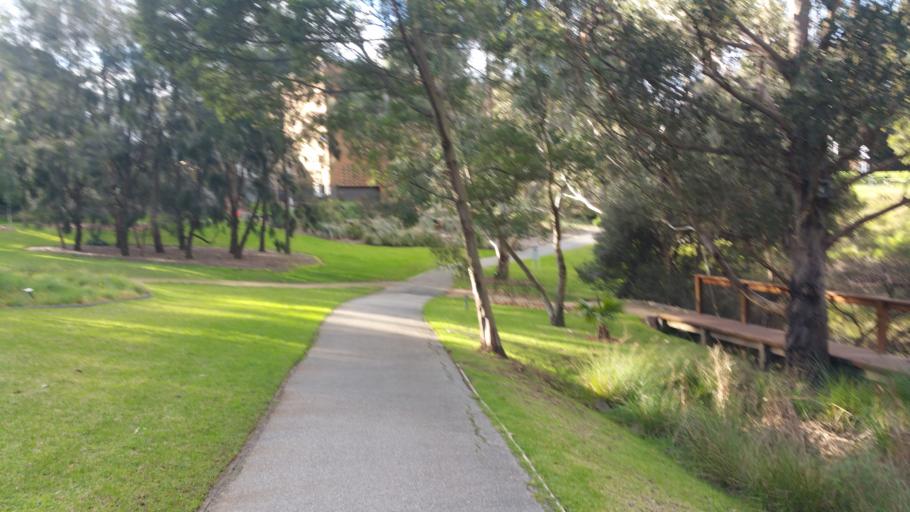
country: AU
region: Victoria
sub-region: Monash
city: Notting Hill
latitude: -37.9079
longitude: 145.1373
